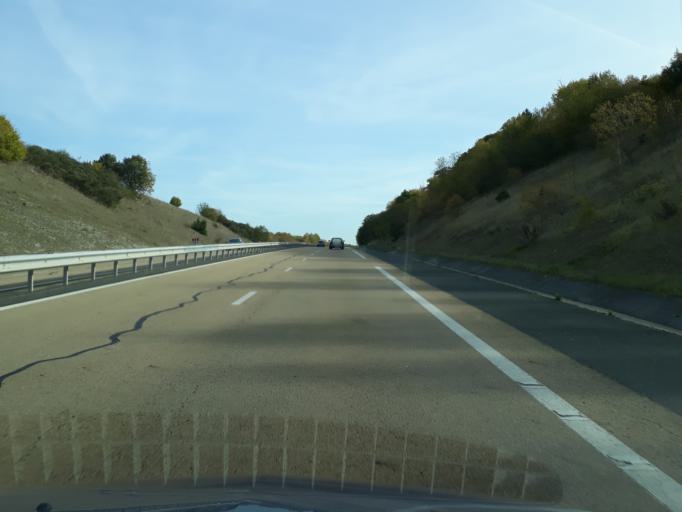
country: FR
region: Champagne-Ardenne
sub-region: Departement de l'Aube
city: Aix-en-Othe
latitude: 48.2574
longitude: 3.6457
